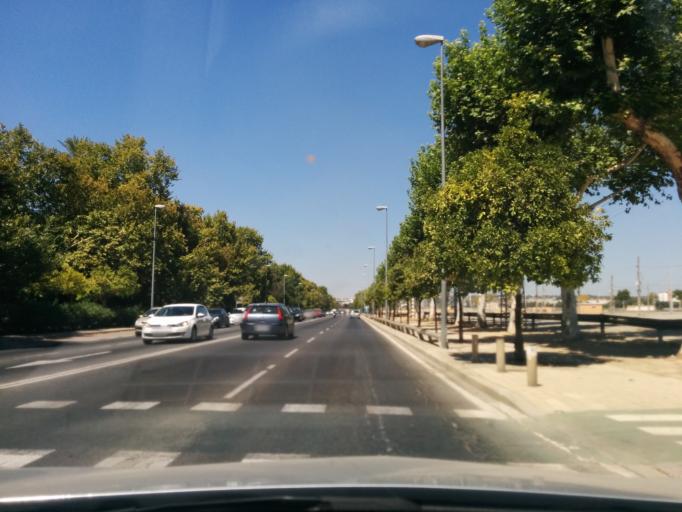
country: ES
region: Andalusia
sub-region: Provincia de Sevilla
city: San Juan de Aznalfarache
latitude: 37.3689
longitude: -6.0047
